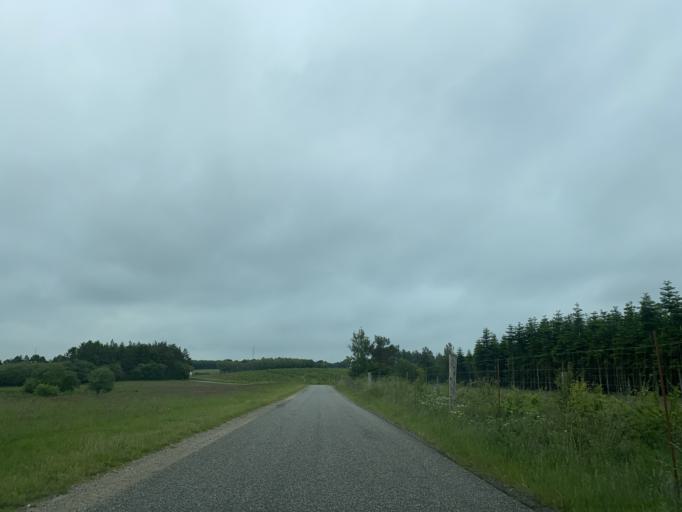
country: DK
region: Central Jutland
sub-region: Viborg Kommune
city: Bjerringbro
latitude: 56.3547
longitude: 9.6265
